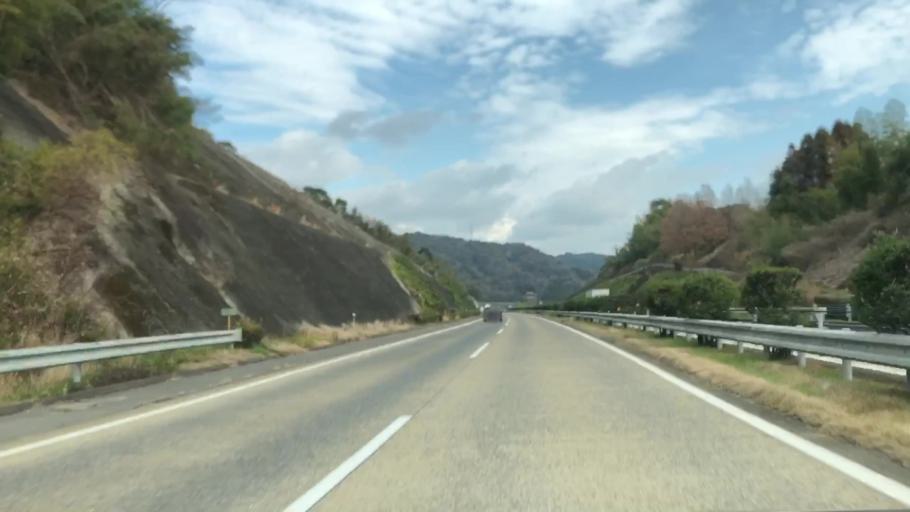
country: JP
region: Saga Prefecture
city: Kanzakimachi-kanzaki
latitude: 33.3331
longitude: 130.3230
